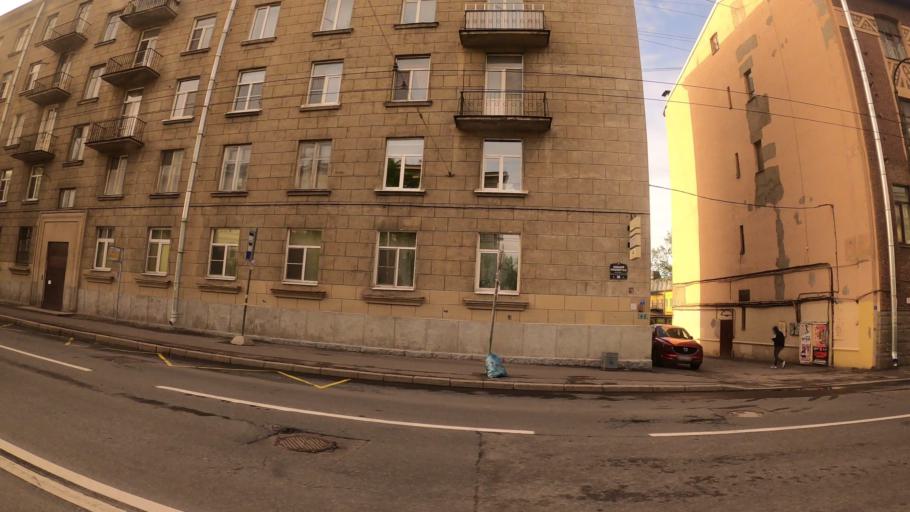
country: RU
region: St.-Petersburg
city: Vasyl'evsky Ostrov
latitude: 59.9292
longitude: 30.2489
